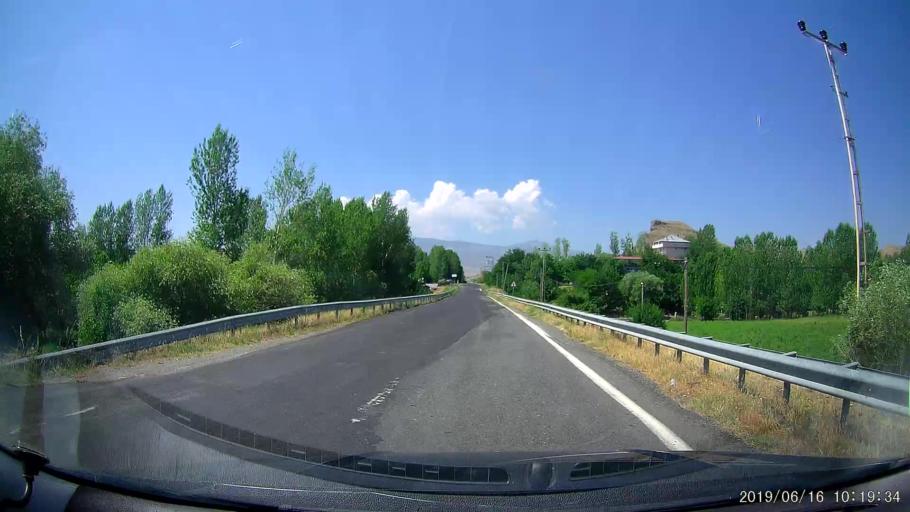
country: TR
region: Igdir
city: Tuzluca
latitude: 40.1543
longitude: 43.6552
